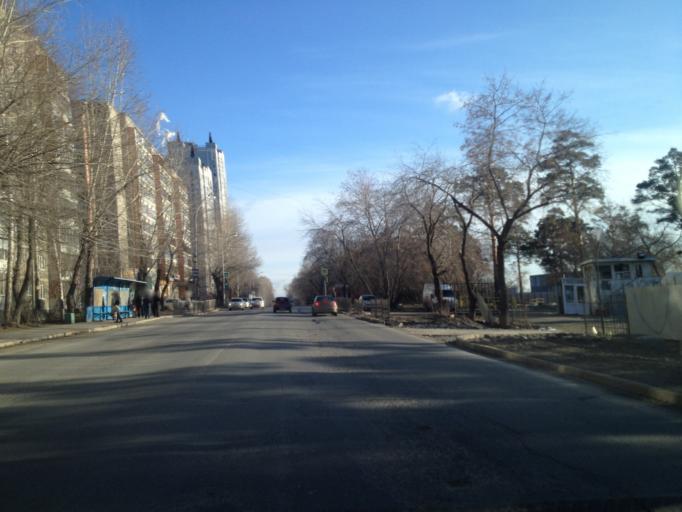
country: RU
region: Sverdlovsk
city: Sovkhoznyy
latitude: 56.7610
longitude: 60.6117
